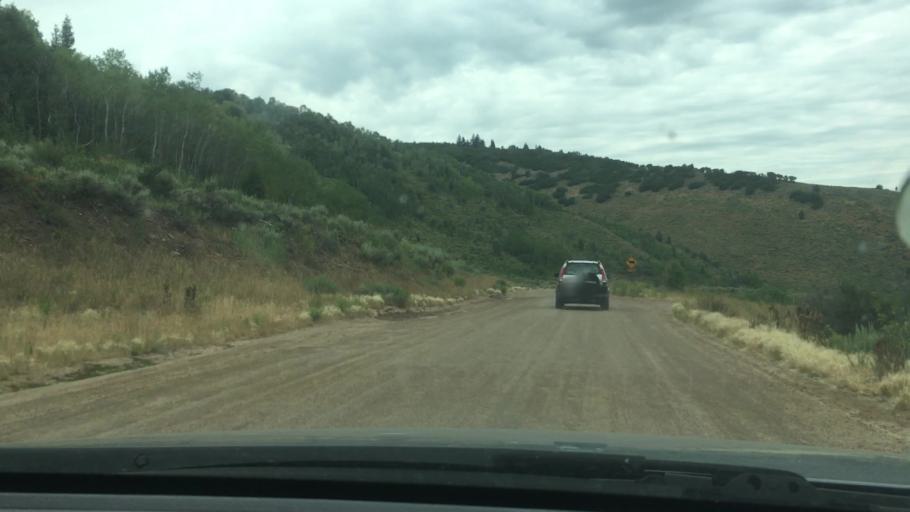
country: US
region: Utah
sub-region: Summit County
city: Summit Park
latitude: 40.7701
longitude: -111.5851
